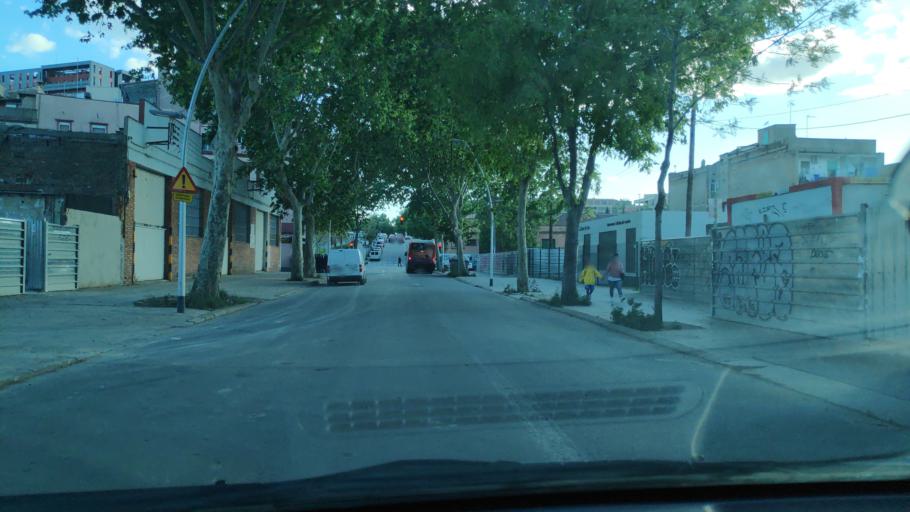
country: ES
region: Catalonia
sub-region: Provincia de Barcelona
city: Sant Marti
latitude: 41.3997
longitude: 2.1890
